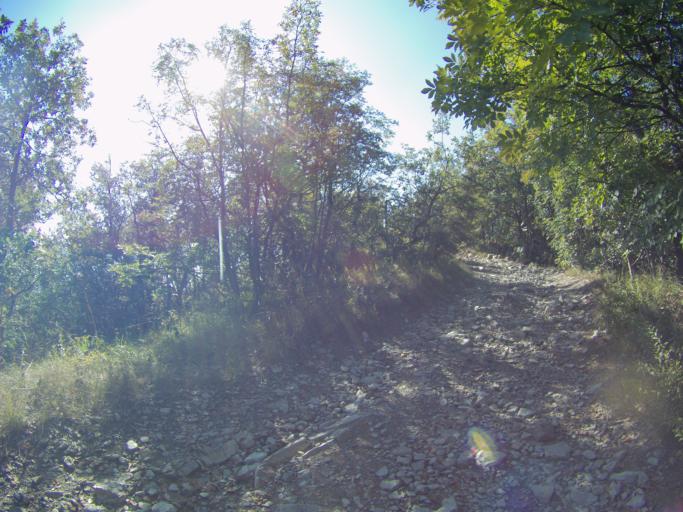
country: IT
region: Emilia-Romagna
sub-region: Provincia di Reggio Emilia
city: Quattro Castella
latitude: 44.5886
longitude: 10.4875
